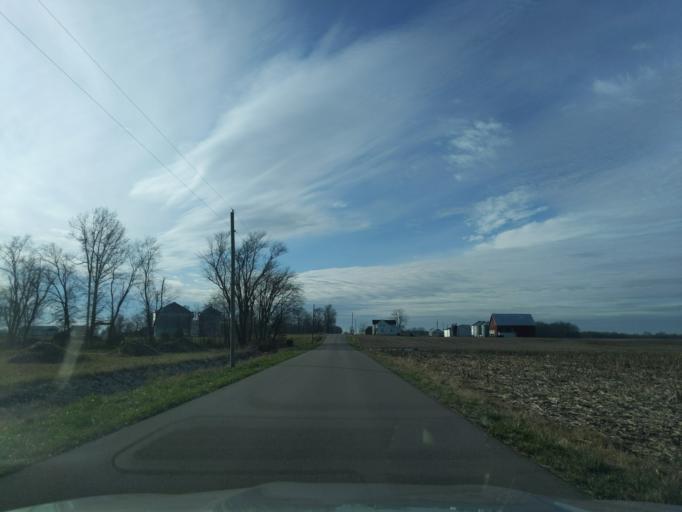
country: US
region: Indiana
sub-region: Decatur County
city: Westport
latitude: 39.1901
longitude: -85.4752
